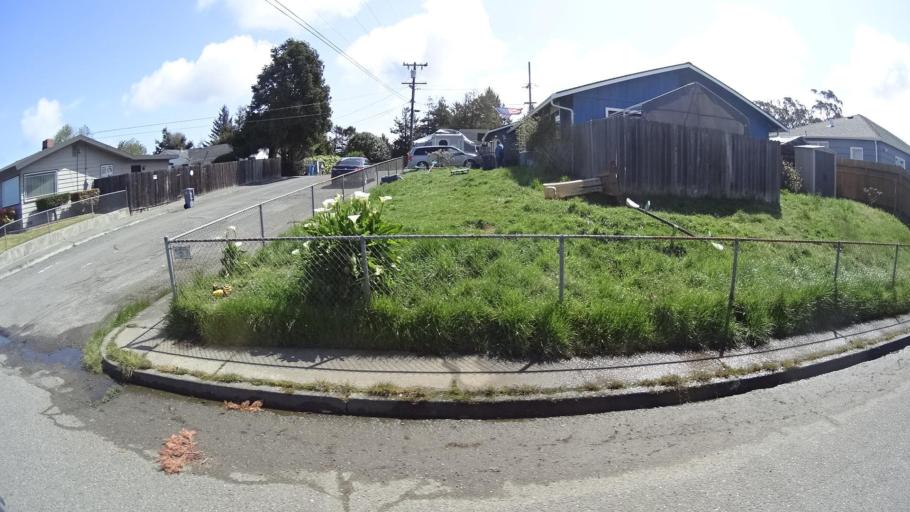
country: US
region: California
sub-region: Humboldt County
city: Bayview
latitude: 40.7712
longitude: -124.1820
